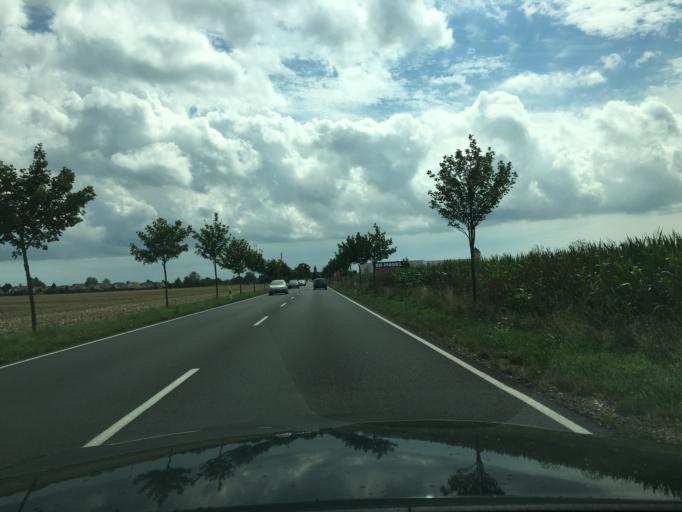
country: DE
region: Saxony-Anhalt
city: Bobbau
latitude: 51.6985
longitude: 12.2593
